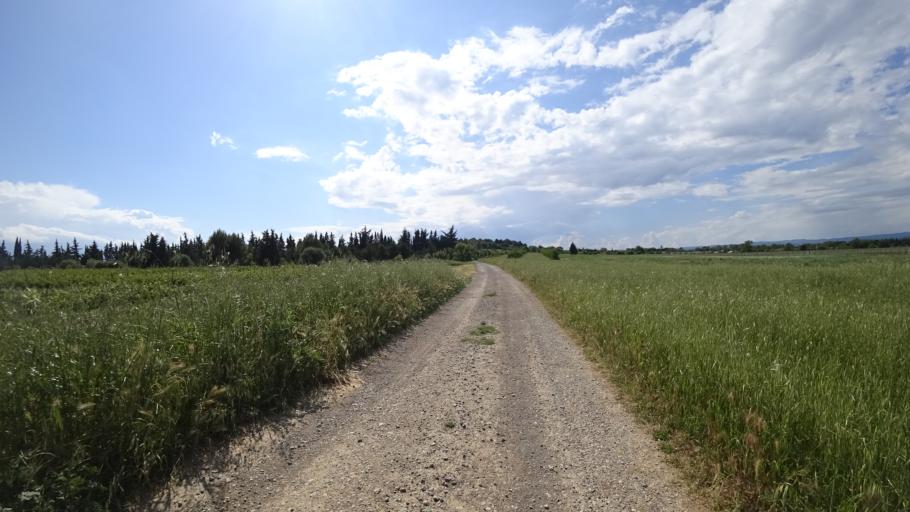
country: FR
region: Languedoc-Roussillon
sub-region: Departement de l'Aude
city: Ginestas
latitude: 43.2624
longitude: 2.8851
